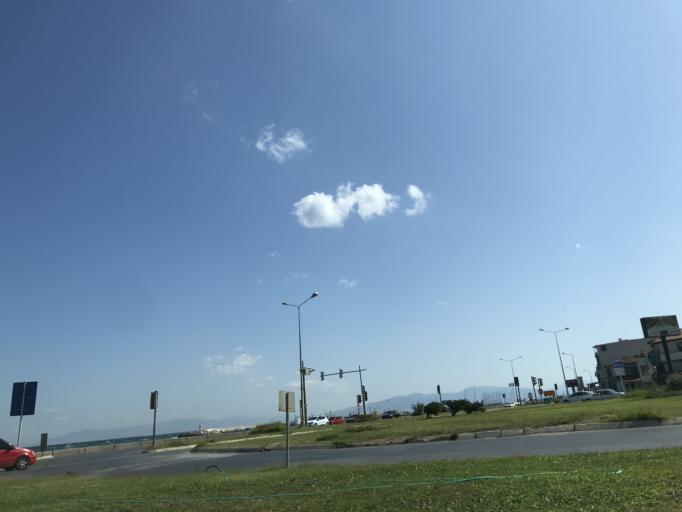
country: TR
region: Izmir
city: Urla
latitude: 38.3752
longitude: 26.8752
